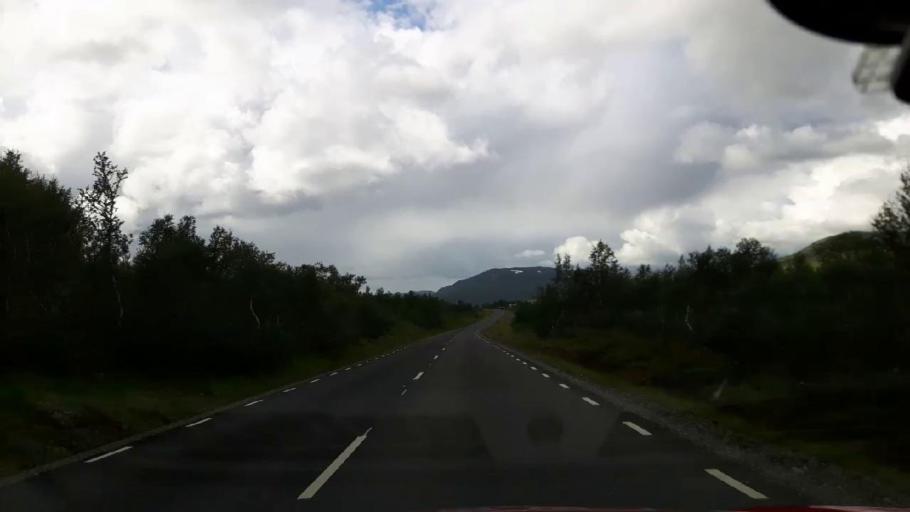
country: NO
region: Nordland
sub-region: Hattfjelldal
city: Hattfjelldal
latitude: 65.0132
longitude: 14.2833
